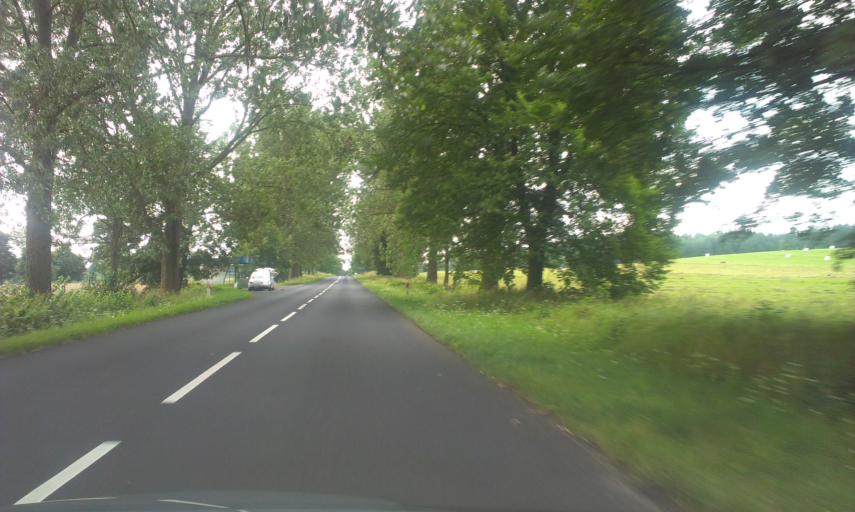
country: PL
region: West Pomeranian Voivodeship
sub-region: Powiat swidwinski
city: Polczyn-Zdroj
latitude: 53.8444
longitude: 16.0755
